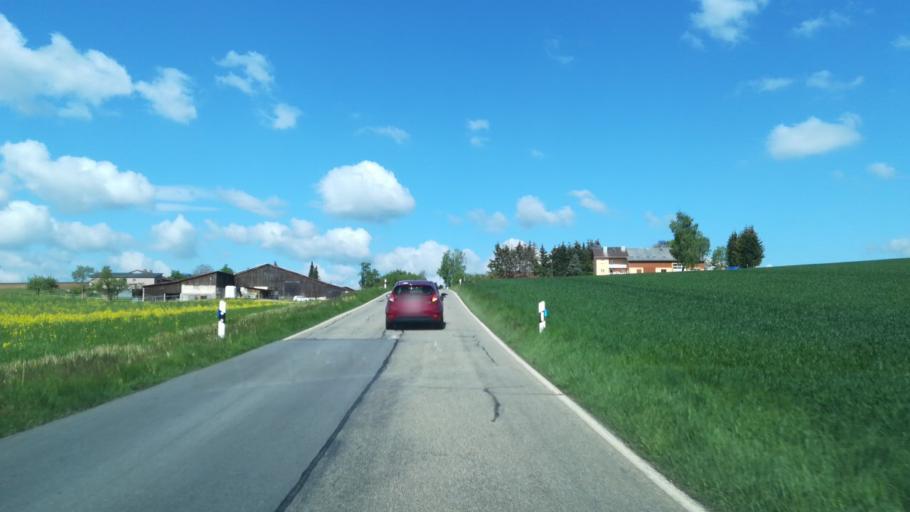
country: DE
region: Baden-Wuerttemberg
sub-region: Freiburg Region
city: Stuhlingen
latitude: 47.7555
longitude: 8.4036
